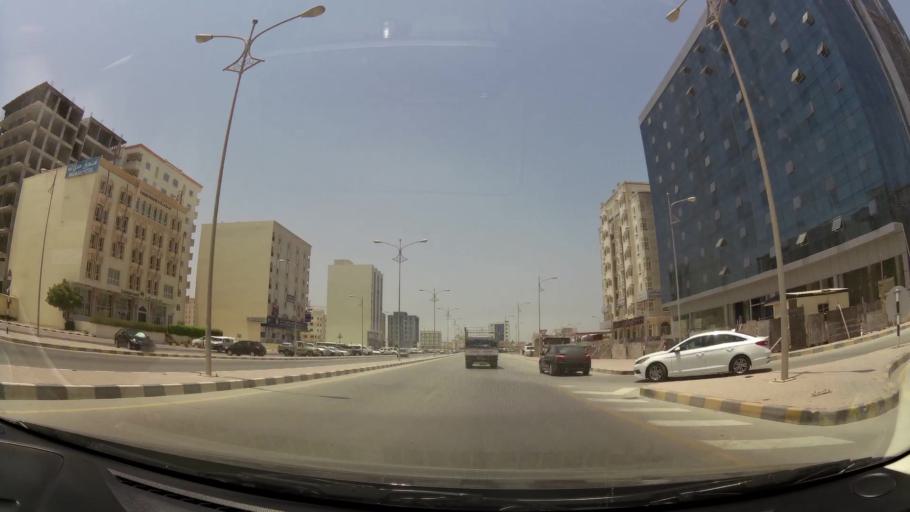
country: OM
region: Zufar
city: Salalah
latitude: 17.0190
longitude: 54.0970
